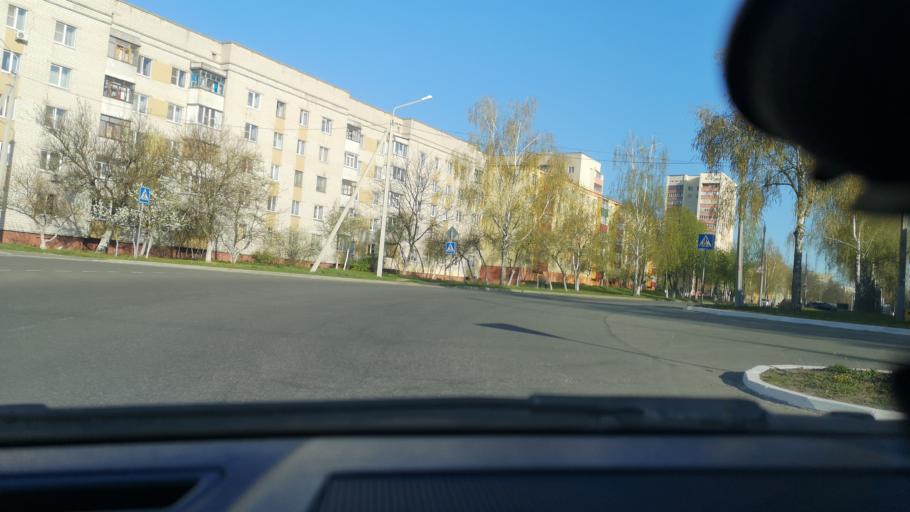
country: BY
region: Gomel
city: Gomel
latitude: 52.4512
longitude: 31.0074
